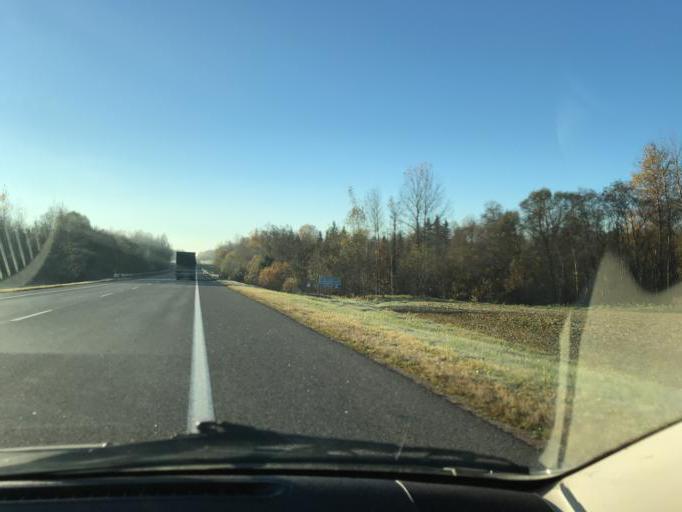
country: BY
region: Vitebsk
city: Vitebsk
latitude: 54.9952
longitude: 30.3393
